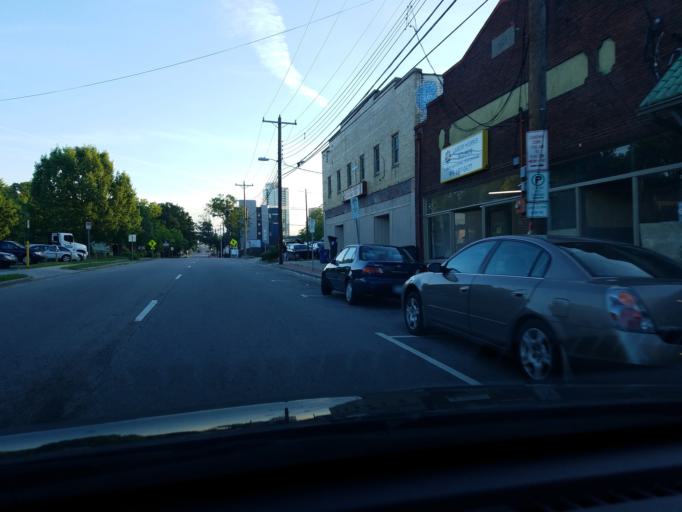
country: US
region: North Carolina
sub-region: Durham County
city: Durham
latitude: 36.0009
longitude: -78.8957
